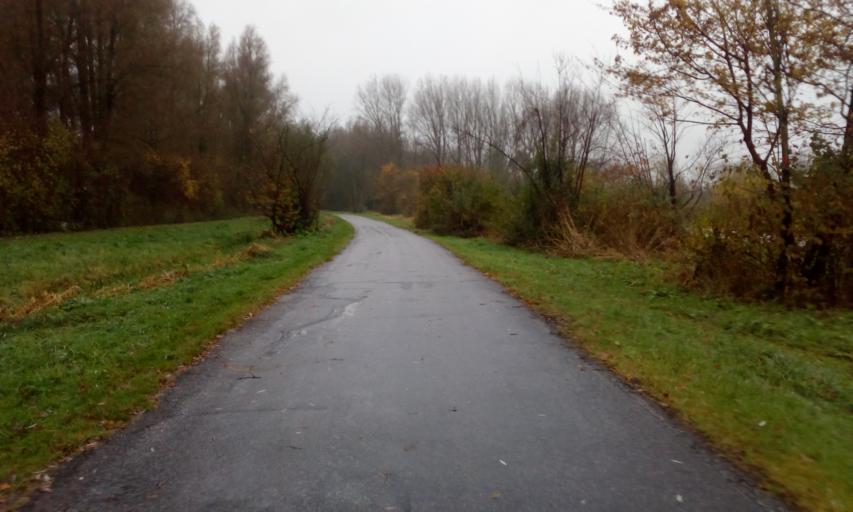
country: NL
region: South Holland
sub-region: Gemeente Lansingerland
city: Bergschenhoek
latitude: 51.9721
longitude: 4.5060
